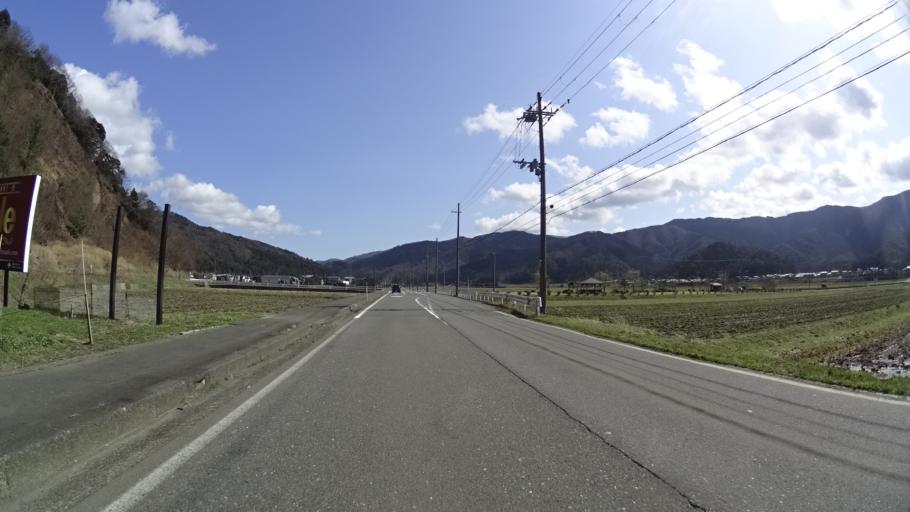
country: JP
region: Fukui
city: Obama
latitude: 35.4628
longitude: 135.8721
